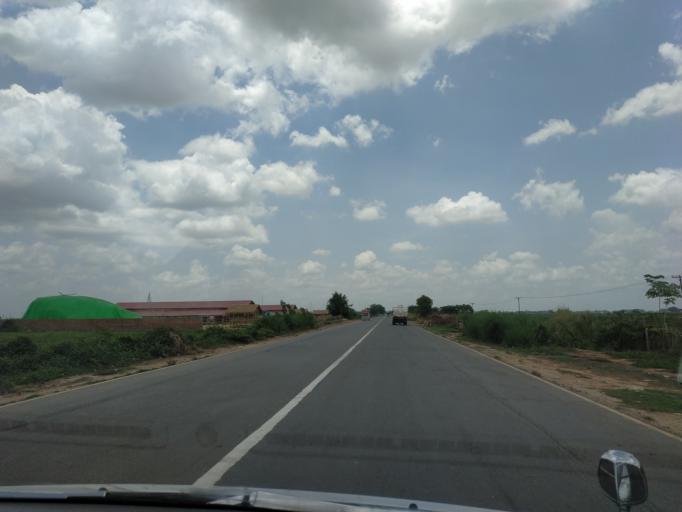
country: MM
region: Bago
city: Bago
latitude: 17.4707
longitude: 96.5532
